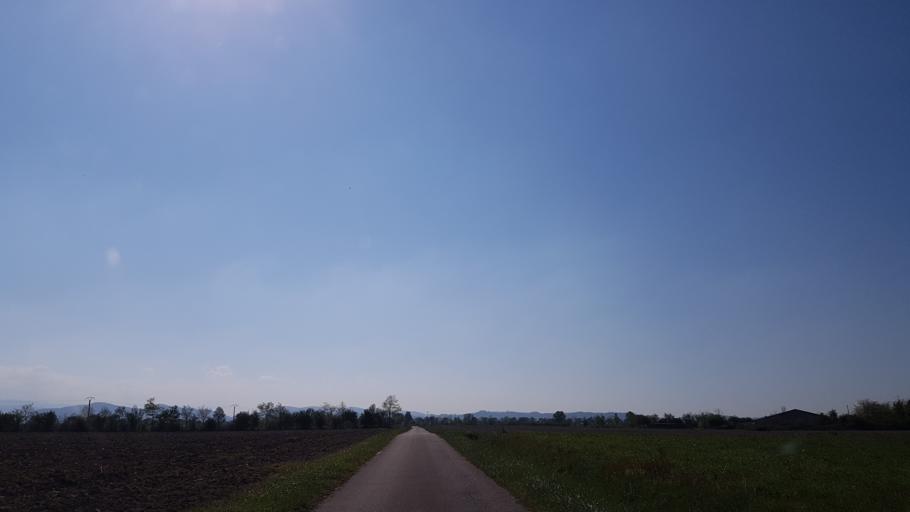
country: FR
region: Midi-Pyrenees
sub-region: Departement de l'Ariege
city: La Tour-du-Crieu
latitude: 43.0871
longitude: 1.6974
